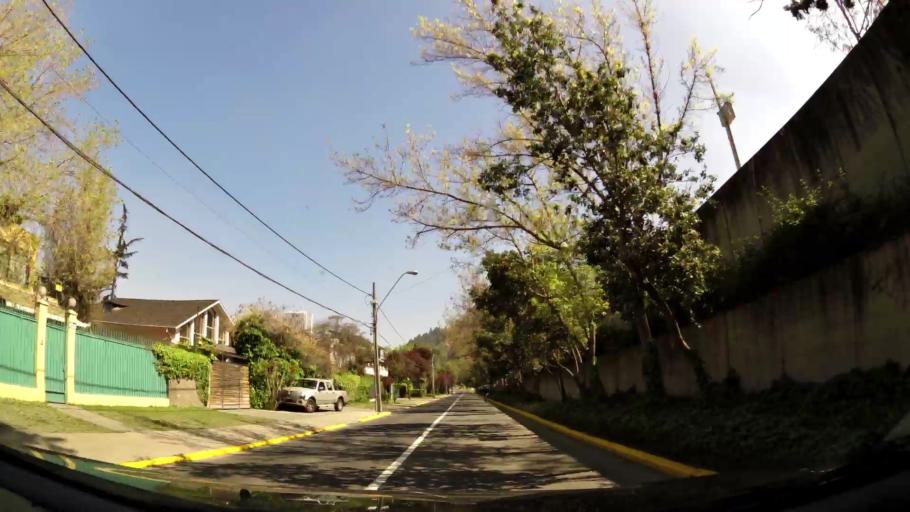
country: CL
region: Santiago Metropolitan
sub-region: Provincia de Santiago
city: Santiago
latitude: -33.4169
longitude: -70.6192
